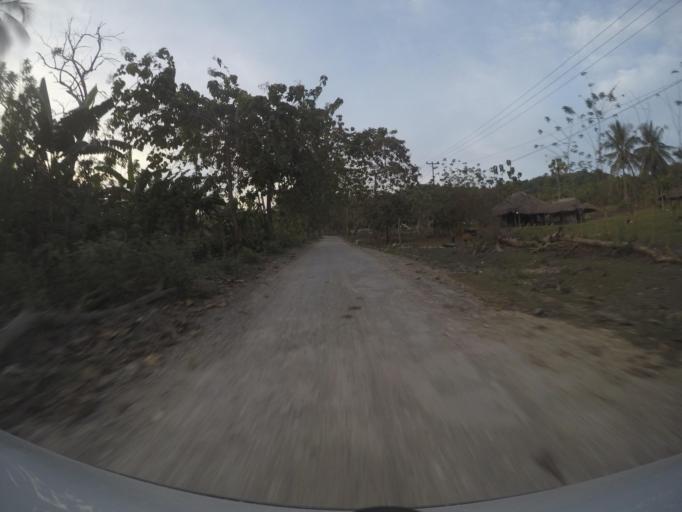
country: TL
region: Viqueque
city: Viqueque
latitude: -8.9159
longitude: 126.3974
